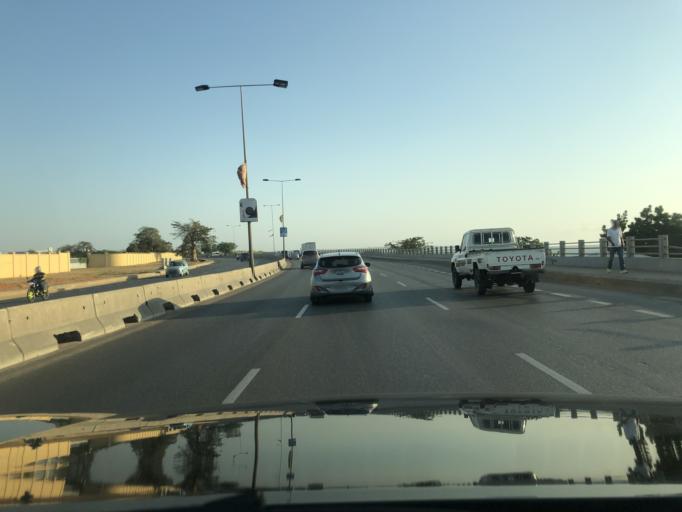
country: AO
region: Luanda
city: Luanda
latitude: -8.9190
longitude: 13.1608
